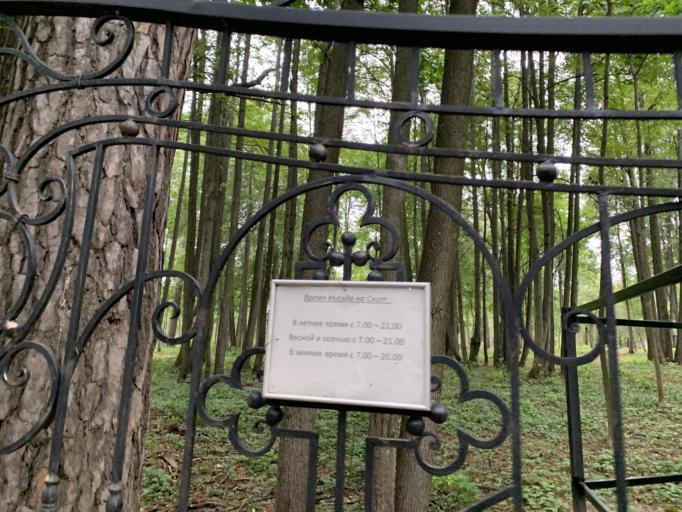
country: RU
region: Moskovskaya
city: Zvenigorod
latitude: 55.7326
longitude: 36.8116
